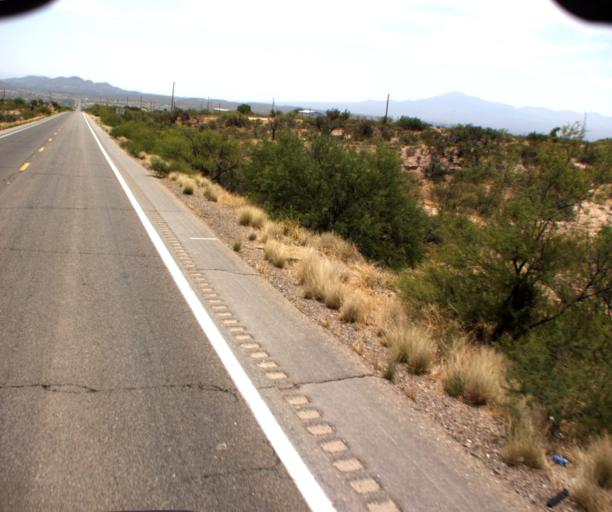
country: US
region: Arizona
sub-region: Gila County
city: Peridot
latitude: 33.3054
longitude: -110.4857
